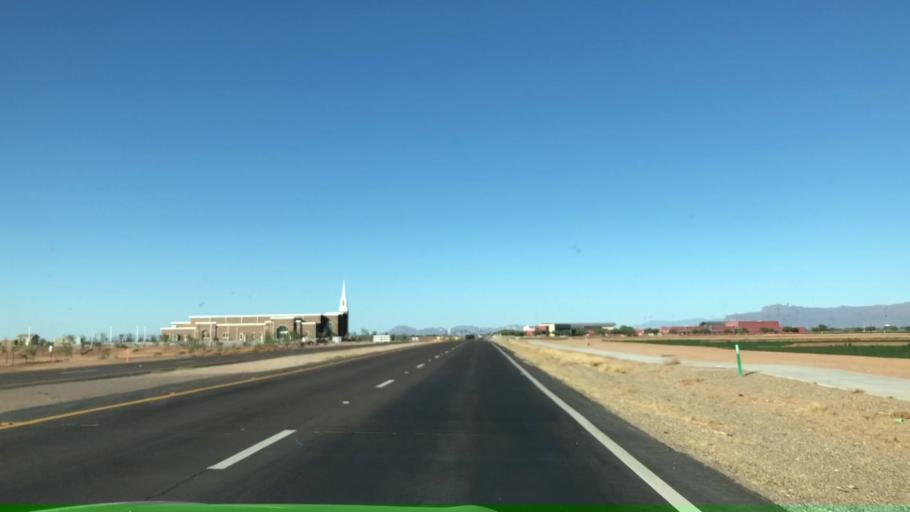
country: US
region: Arizona
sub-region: Pinal County
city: San Tan Valley
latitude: 33.1656
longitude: -111.5450
